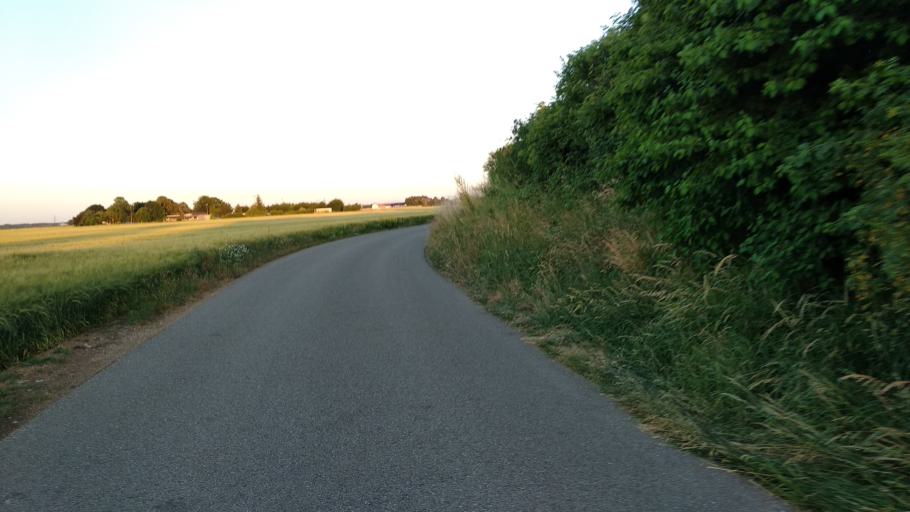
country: DE
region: Bavaria
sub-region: Upper Bavaria
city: Vaterstetten
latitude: 48.1258
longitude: 11.7611
